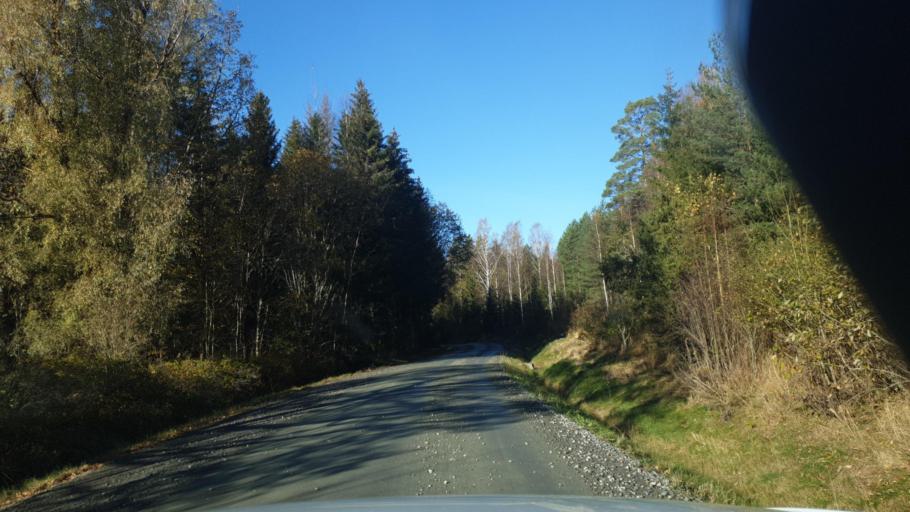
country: SE
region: Vaermland
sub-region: Karlstads Kommun
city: Edsvalla
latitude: 59.4507
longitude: 13.1497
